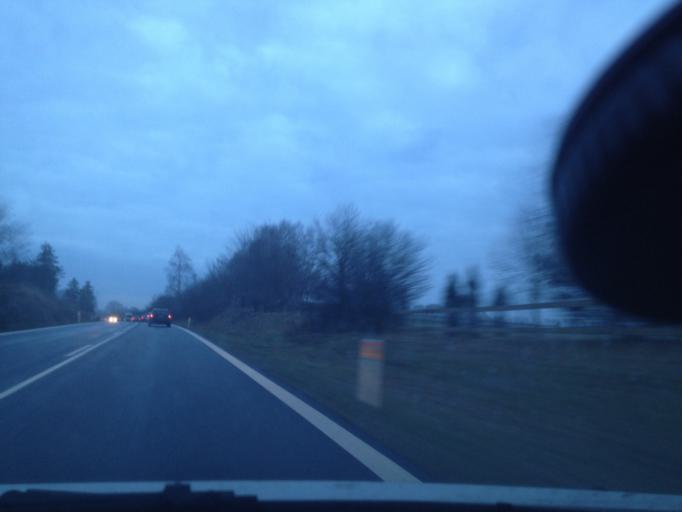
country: DK
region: Capital Region
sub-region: Rudersdal Kommune
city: Birkerod
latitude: 55.8948
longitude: 12.4308
